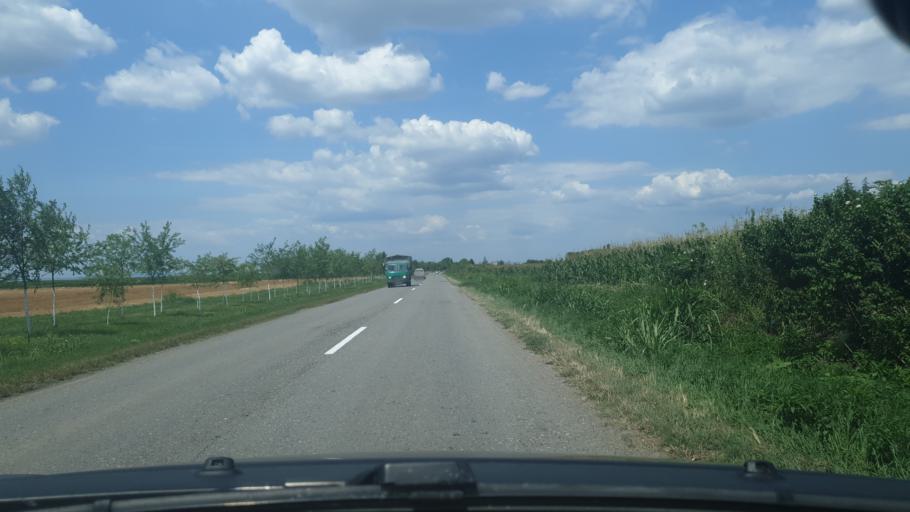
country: RS
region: Autonomna Pokrajina Vojvodina
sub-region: Sremski Okrug
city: Pecinci
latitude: 44.8542
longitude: 19.9610
